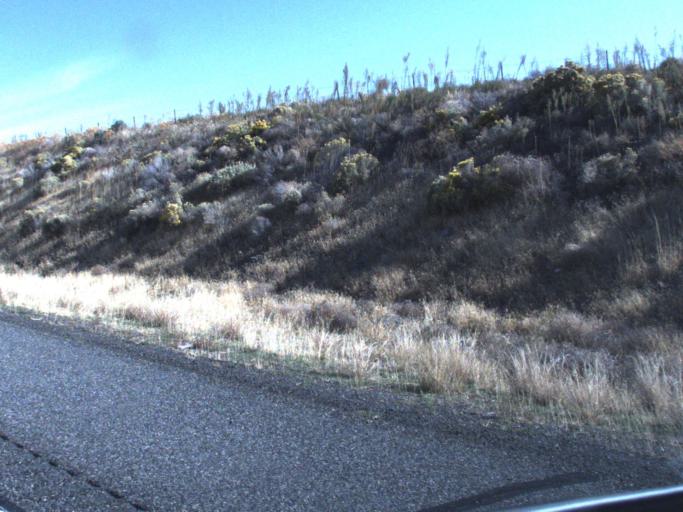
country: US
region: Washington
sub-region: Franklin County
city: West Pasco
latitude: 46.1748
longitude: -119.2215
